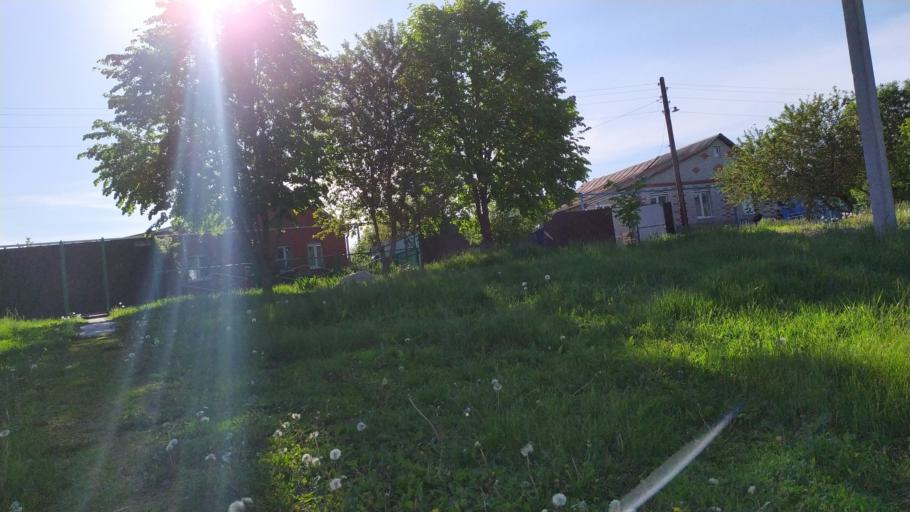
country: RU
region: Kursk
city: Kursk
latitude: 51.6365
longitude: 36.1495
